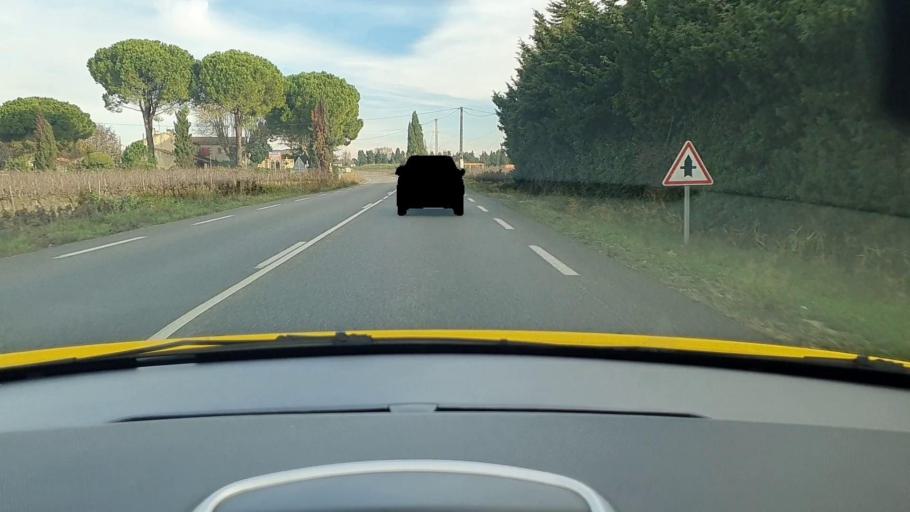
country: FR
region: Languedoc-Roussillon
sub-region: Departement du Gard
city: Beaucaire
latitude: 43.7847
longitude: 4.6270
